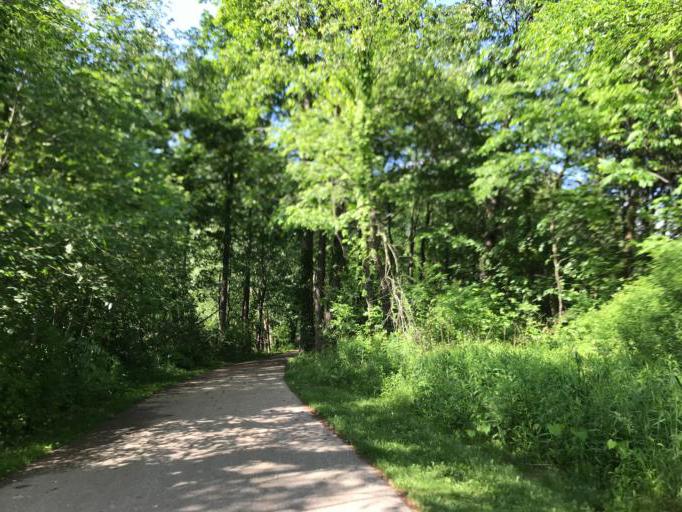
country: US
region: Michigan
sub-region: Oakland County
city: South Lyon
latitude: 42.4344
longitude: -83.6594
